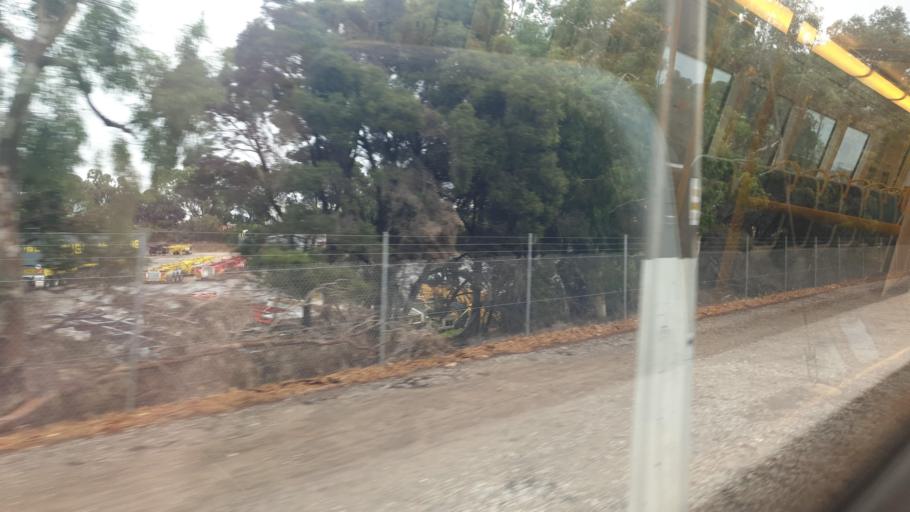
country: AU
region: Western Australia
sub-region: Fremantle
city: North Fremantle
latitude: -32.0351
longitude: 115.7516
